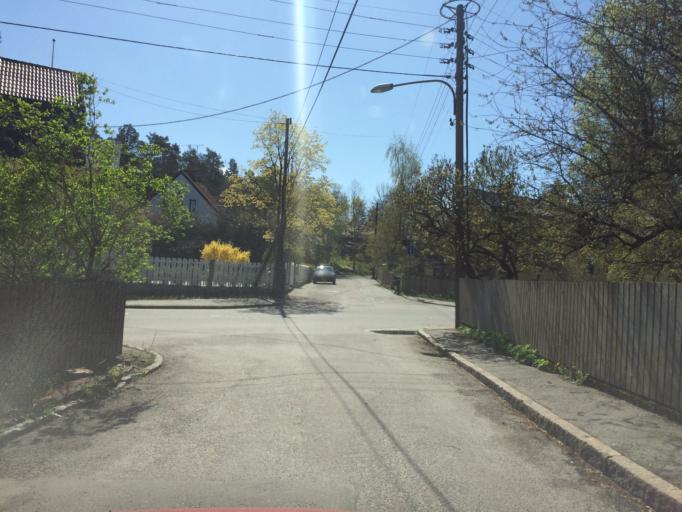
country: SE
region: Stockholm
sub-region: Huddinge Kommun
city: Segeltorp
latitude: 59.3000
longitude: 17.9582
